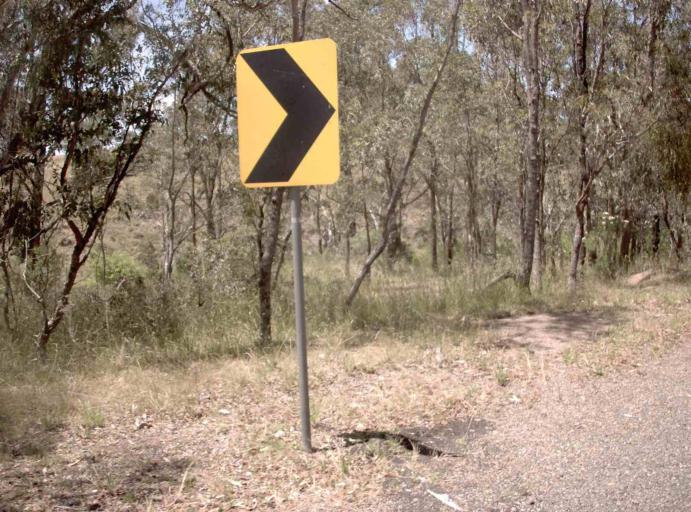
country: AU
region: Victoria
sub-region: East Gippsland
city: Bairnsdale
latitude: -37.4007
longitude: 147.8361
